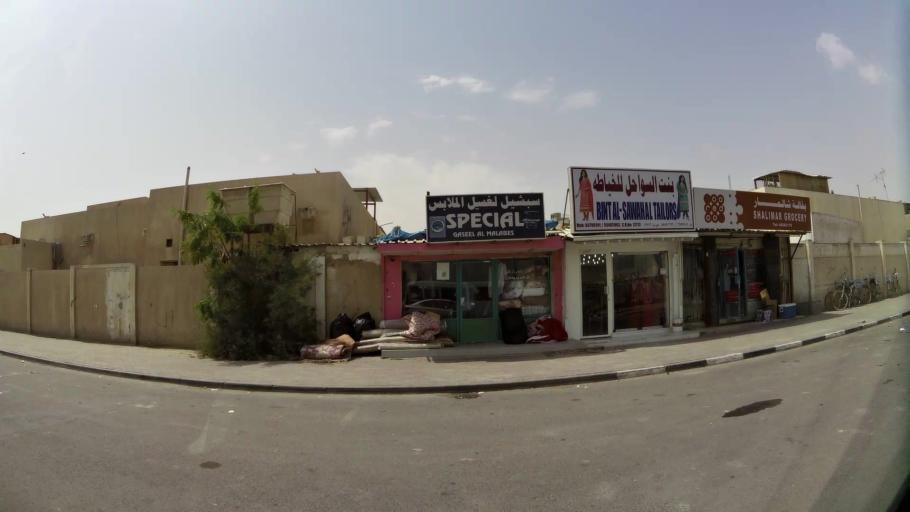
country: QA
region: Baladiyat ar Rayyan
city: Ar Rayyan
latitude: 25.2417
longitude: 51.4262
